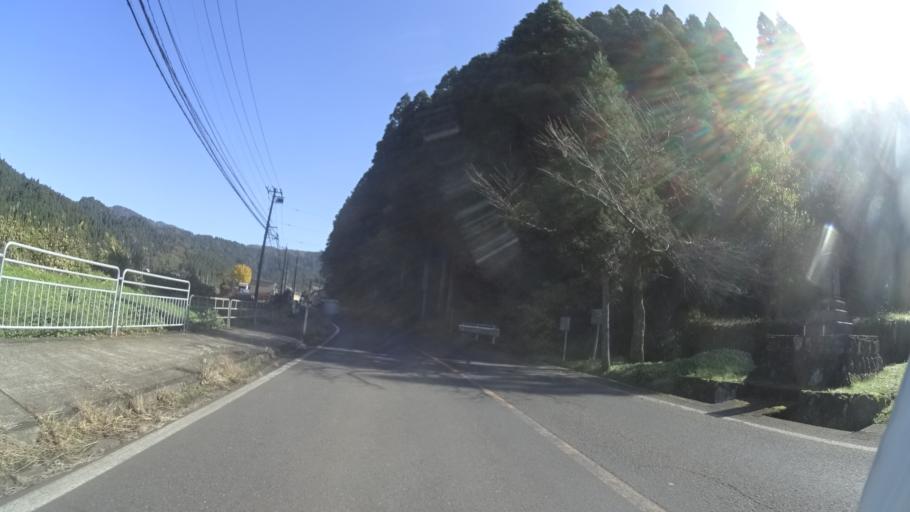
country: JP
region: Fukui
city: Sabae
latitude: 35.9355
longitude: 136.2931
